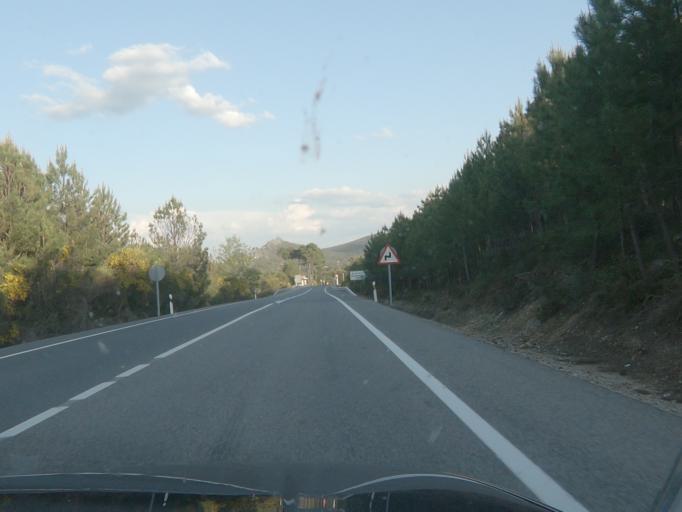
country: PT
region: Portalegre
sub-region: Portalegre
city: Sao Juliao
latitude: 39.3483
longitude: -7.3015
